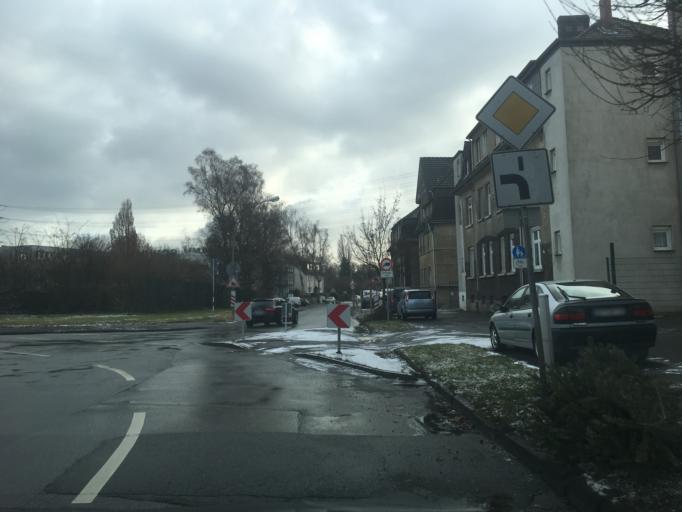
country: DE
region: North Rhine-Westphalia
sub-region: Regierungsbezirk Munster
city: Bottrop
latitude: 51.5107
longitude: 6.9425
